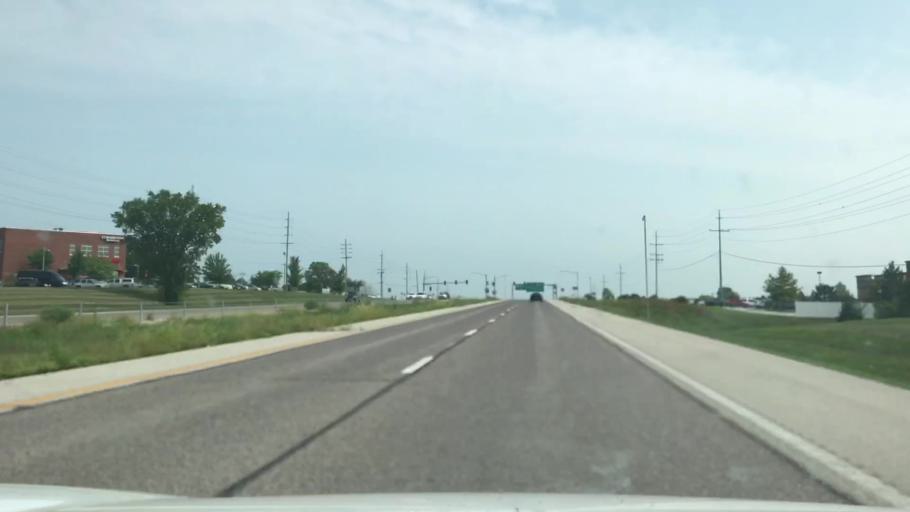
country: US
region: Missouri
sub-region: Saint Charles County
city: Cottleville
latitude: 38.7296
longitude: -90.6422
